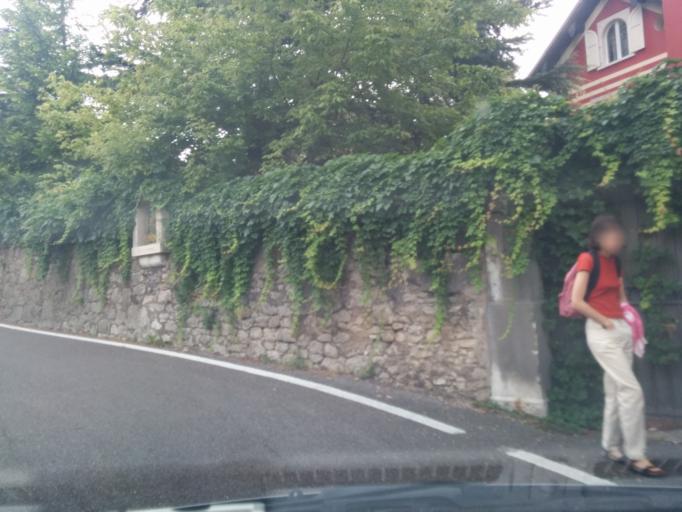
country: IT
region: Trentino-Alto Adige
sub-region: Provincia di Trento
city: Trento
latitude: 46.0716
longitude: 11.1310
